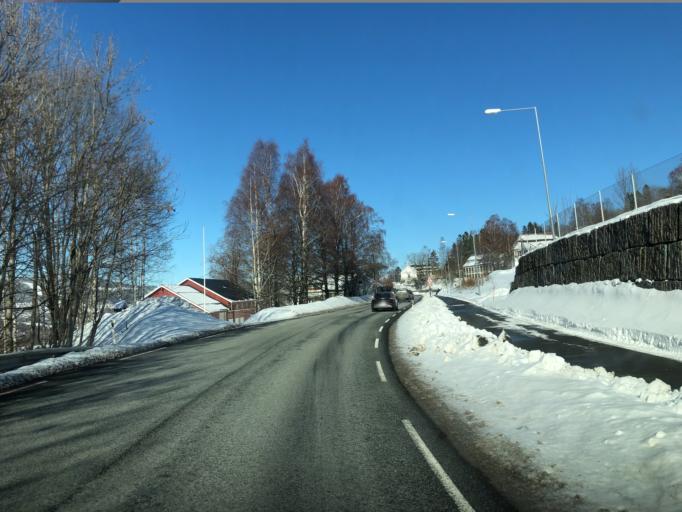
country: NO
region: Buskerud
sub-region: Lier
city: Tranby
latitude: 59.8263
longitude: 10.2558
